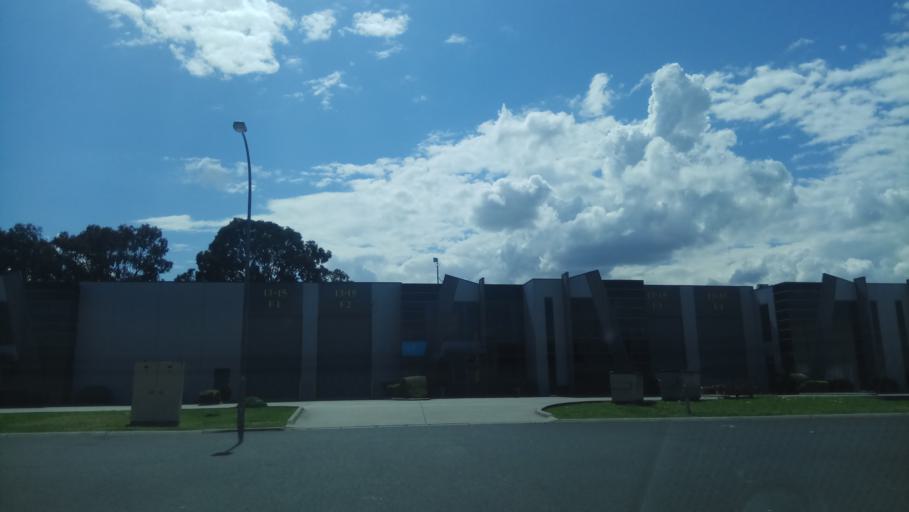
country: AU
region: Victoria
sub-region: Kingston
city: Dingley Village
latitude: -37.9937
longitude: 145.1171
